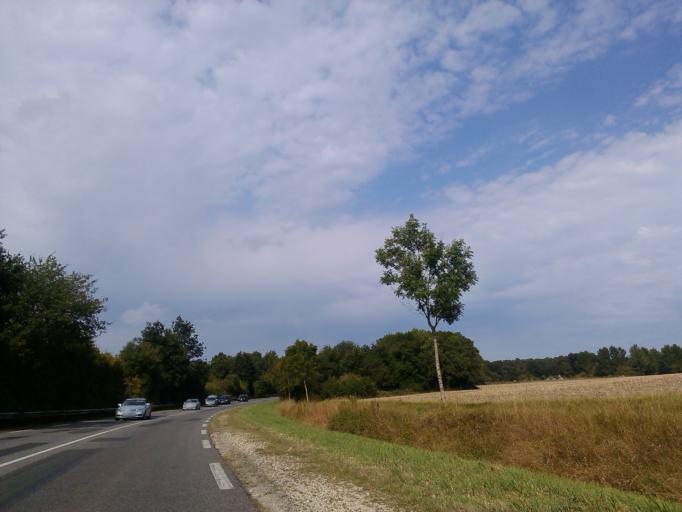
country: FR
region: Poitou-Charentes
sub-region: Departement de la Charente-Maritime
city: La Tremblade
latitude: 45.7562
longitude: -1.1519
